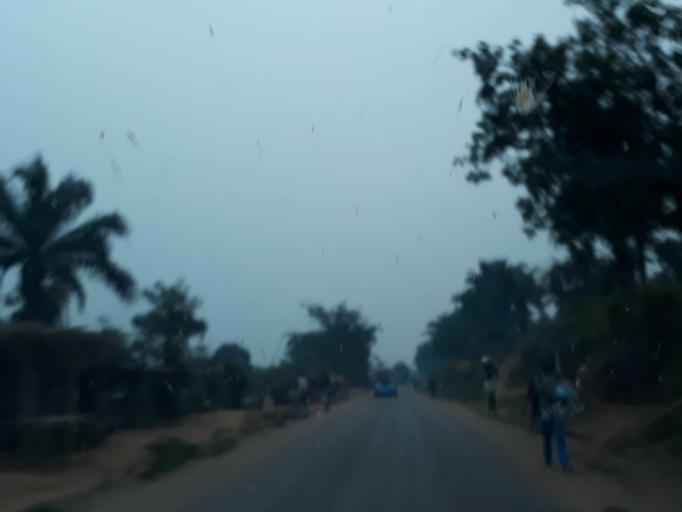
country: CD
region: Bandundu
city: Kikwit
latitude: -5.0594
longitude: 18.8571
